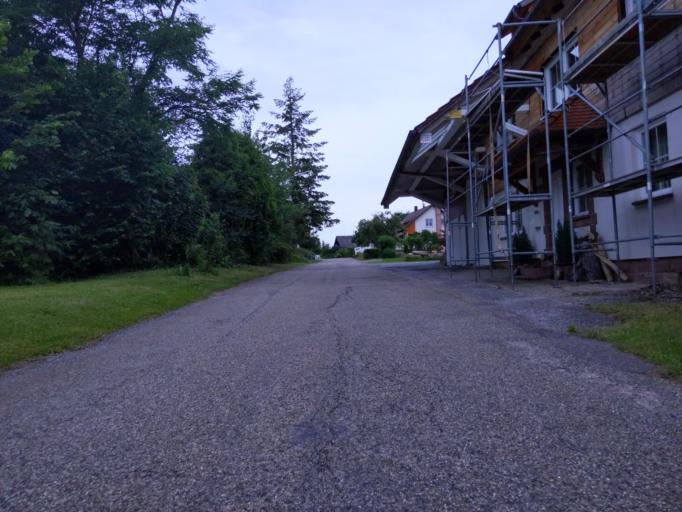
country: DE
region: Baden-Wuerttemberg
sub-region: Karlsruhe Region
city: Alpirsbach
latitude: 48.3371
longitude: 8.4332
